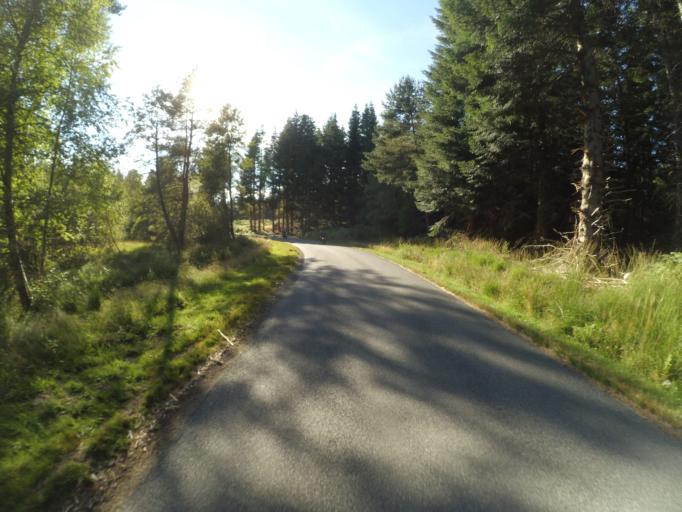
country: FR
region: Limousin
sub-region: Departement de la Creuse
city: Banize
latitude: 45.7911
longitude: 1.9528
